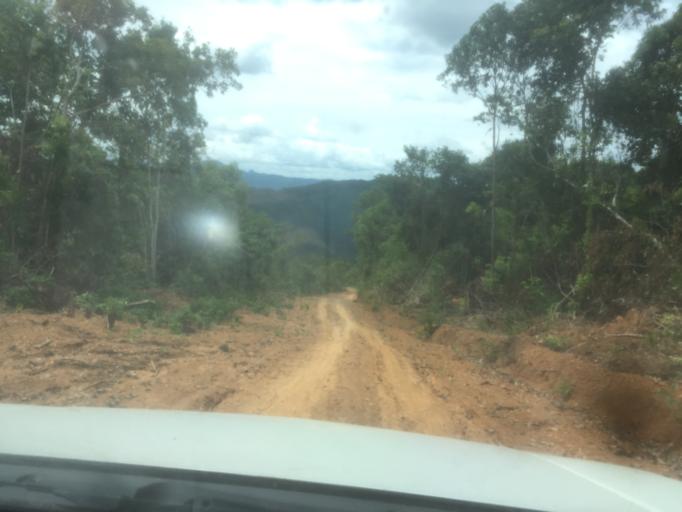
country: LA
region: Phongsali
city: Khoa
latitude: 20.9236
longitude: 102.5538
